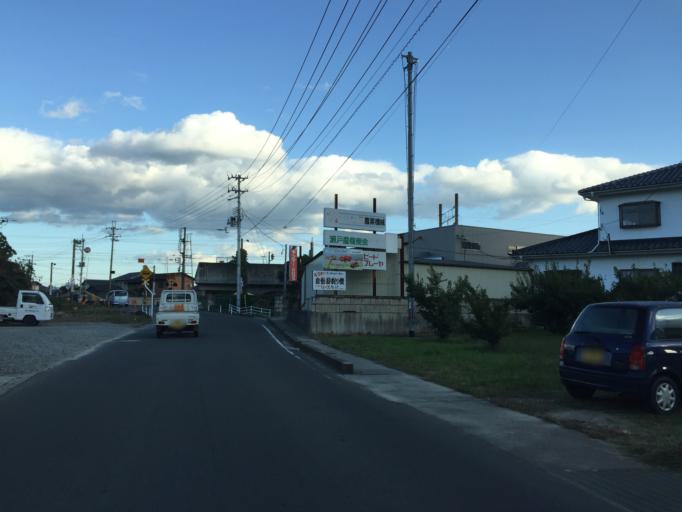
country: JP
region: Fukushima
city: Fukushima-shi
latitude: 37.8066
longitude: 140.4826
